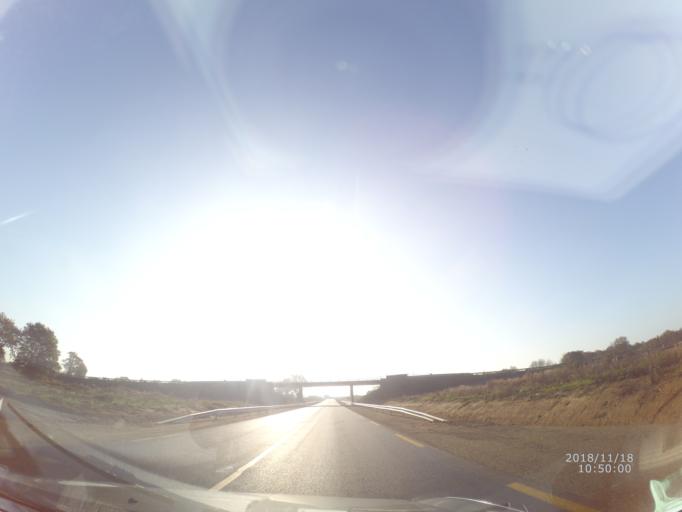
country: FR
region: Pays de la Loire
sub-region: Departement de la Loire-Atlantique
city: Vue
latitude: 47.2006
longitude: -1.9184
